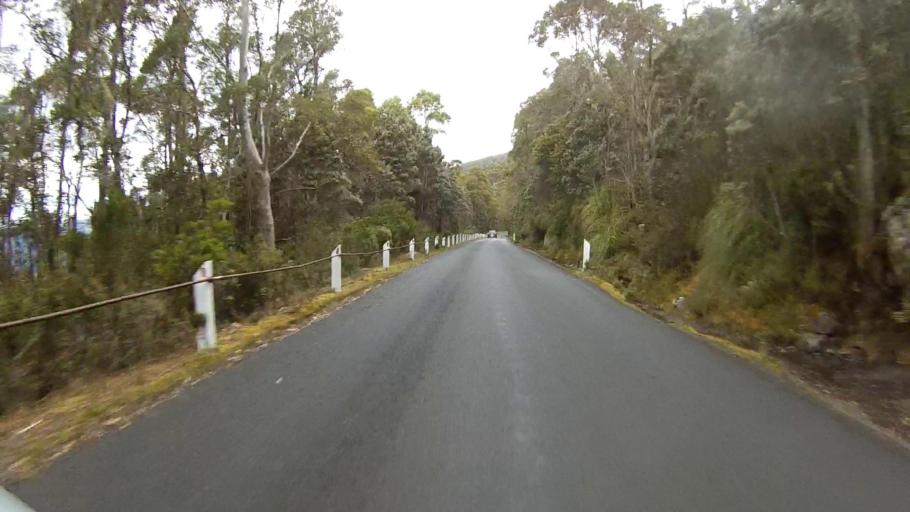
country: AU
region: Tasmania
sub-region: Glenorchy
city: West Moonah
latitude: -42.9005
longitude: 147.2439
